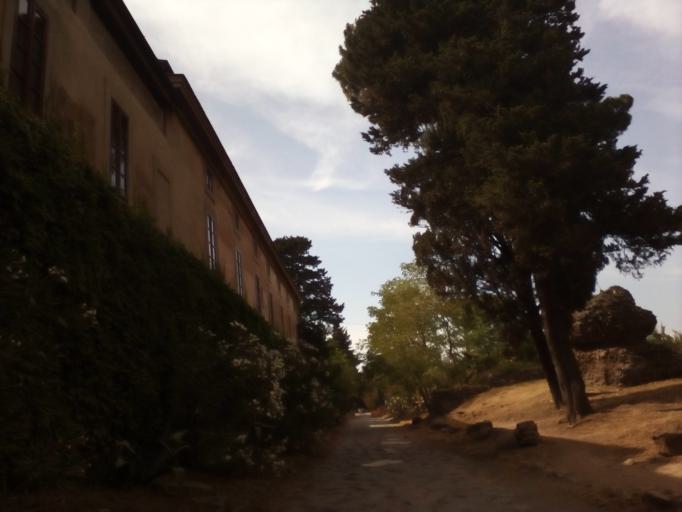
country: IT
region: Latium
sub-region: Citta metropolitana di Roma Capitale
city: Rome
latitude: 41.8450
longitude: 12.5287
